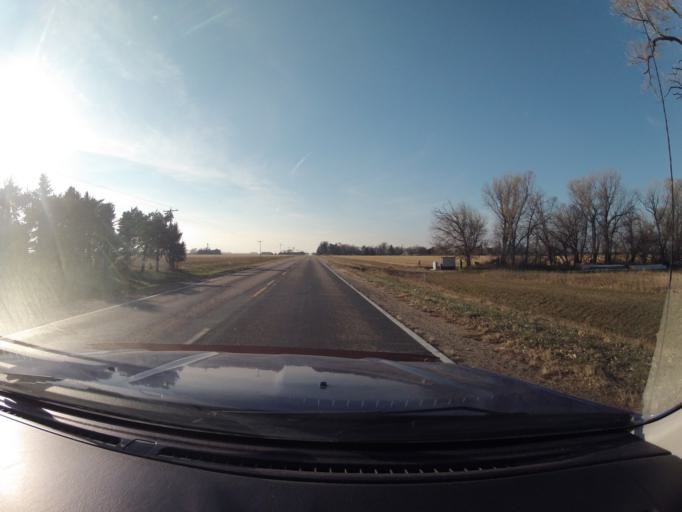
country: US
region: Nebraska
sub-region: Buffalo County
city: Kearney
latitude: 40.6410
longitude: -98.9984
